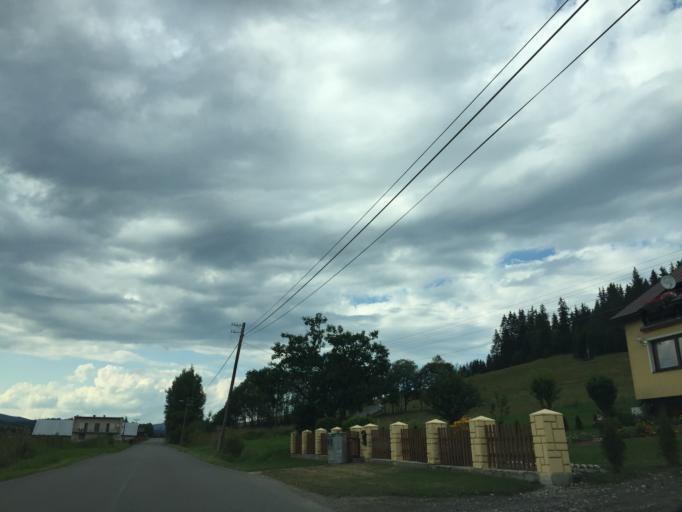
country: PL
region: Silesian Voivodeship
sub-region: Powiat zywiecki
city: Sopotnia Wielka
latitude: 49.4400
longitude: 19.3133
